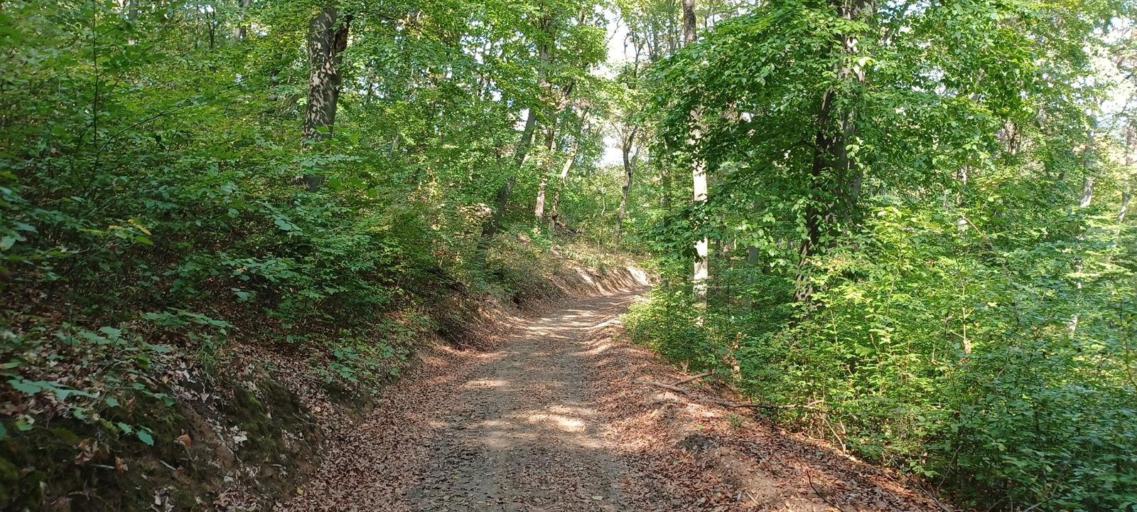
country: HU
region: Tolna
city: Szentgalpuszta
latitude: 46.3257
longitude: 18.6248
